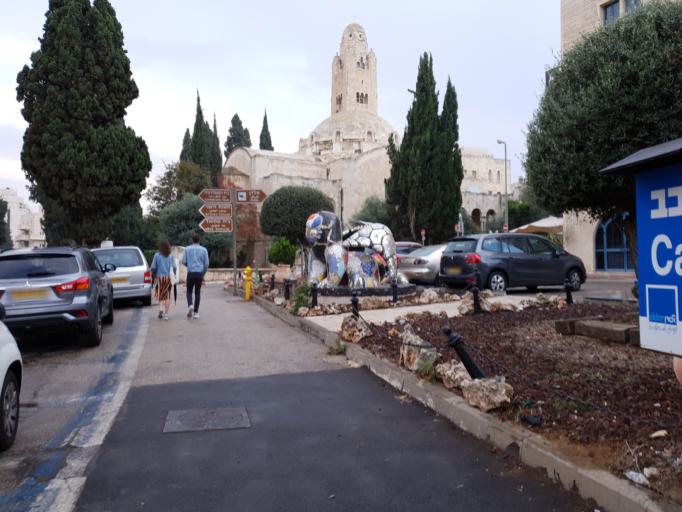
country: IL
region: Jerusalem
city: West Jerusalem
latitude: 31.7752
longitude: 35.2219
